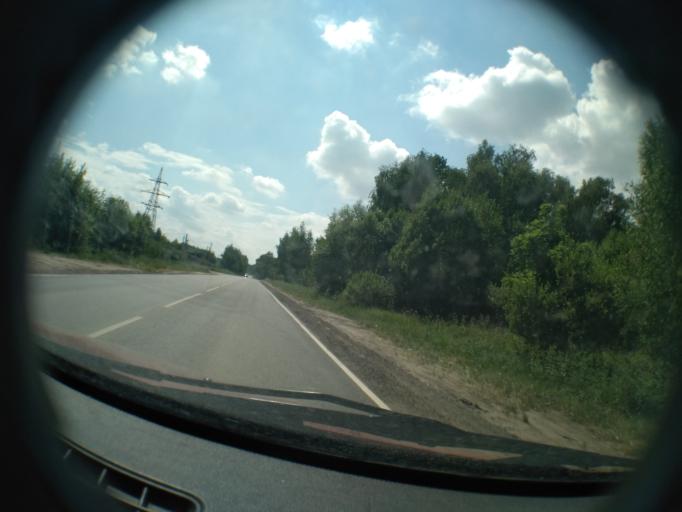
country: RU
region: Moskovskaya
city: Ostrovtsy
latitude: 55.5083
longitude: 38.0078
